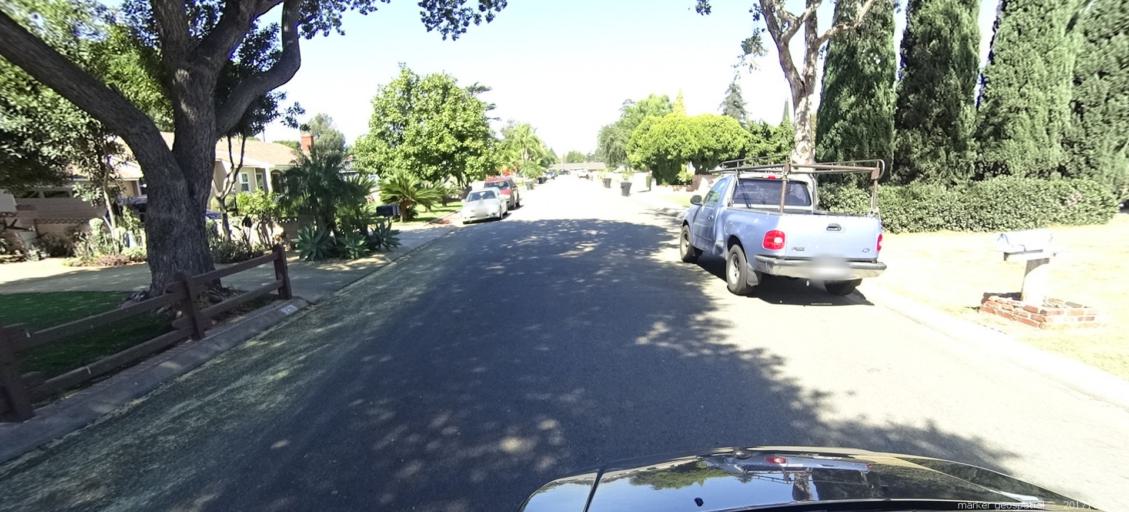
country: US
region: California
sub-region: Orange County
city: Garden Grove
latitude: 33.7825
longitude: -117.9697
